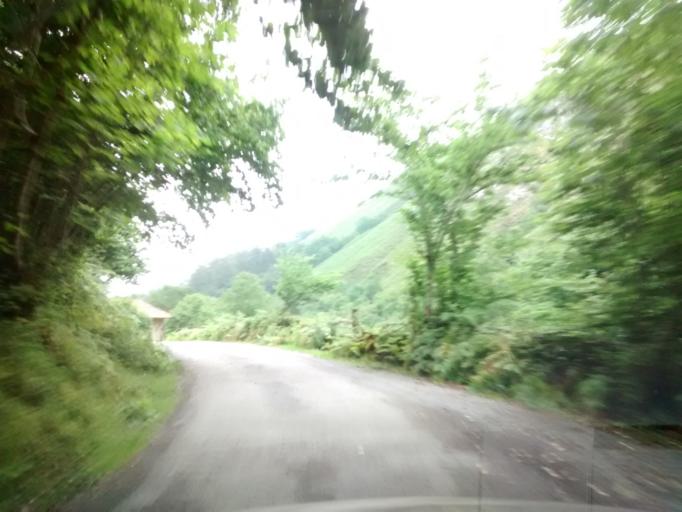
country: ES
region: Asturias
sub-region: Province of Asturias
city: Pilona
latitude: 43.2746
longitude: -5.3488
